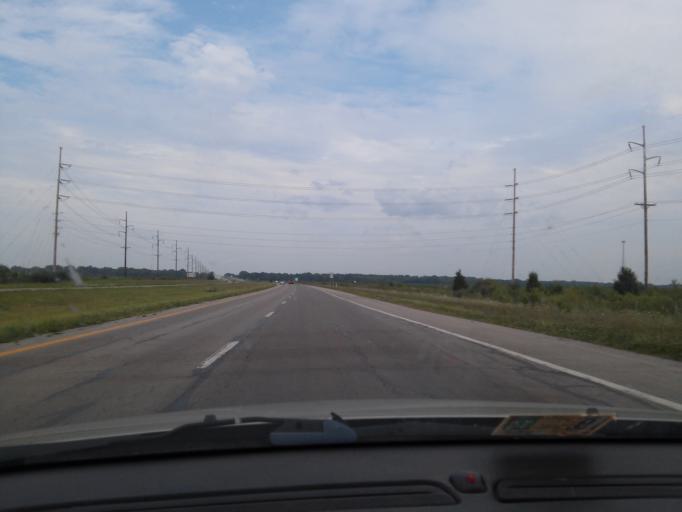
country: US
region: Ohio
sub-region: Fayette County
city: Washington Court House
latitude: 39.5131
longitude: -83.4357
